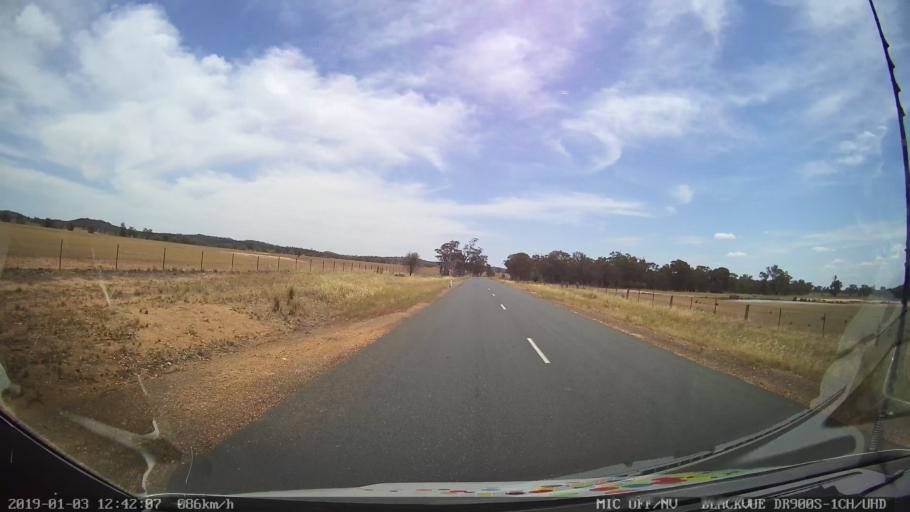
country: AU
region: New South Wales
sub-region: Weddin
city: Grenfell
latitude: -33.7910
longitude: 148.2133
